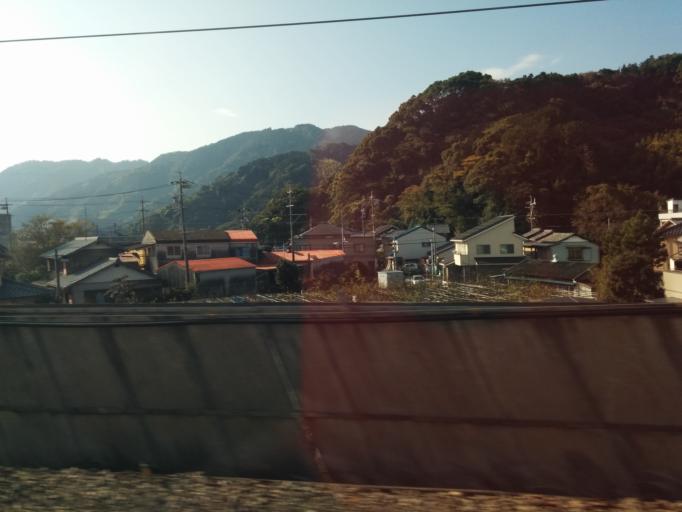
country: JP
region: Shizuoka
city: Shizuoka-shi
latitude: 34.9338
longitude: 138.3630
